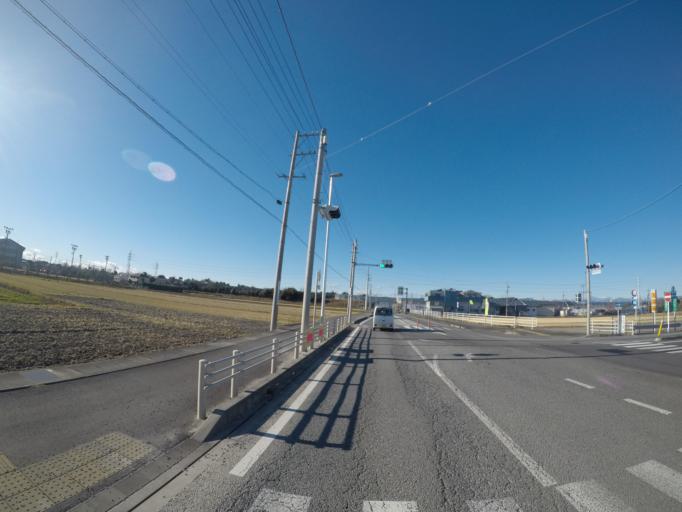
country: JP
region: Shizuoka
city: Fujieda
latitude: 34.8158
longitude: 138.2669
